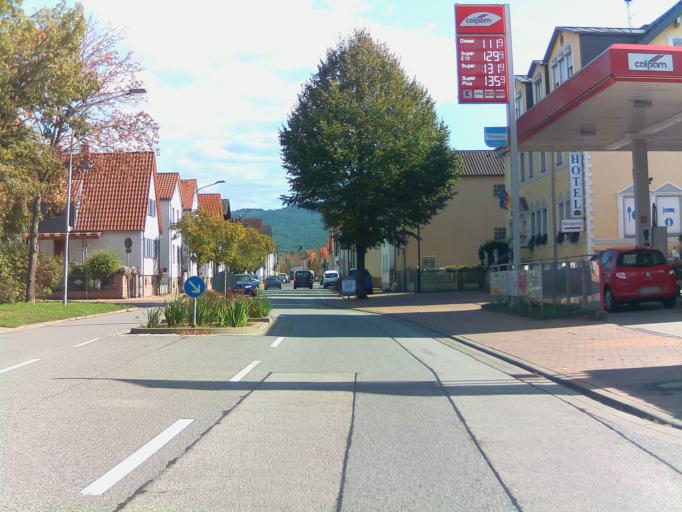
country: DE
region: Hesse
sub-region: Regierungsbezirk Darmstadt
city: Alsbach-Hahnlein
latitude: 49.7367
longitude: 8.5659
